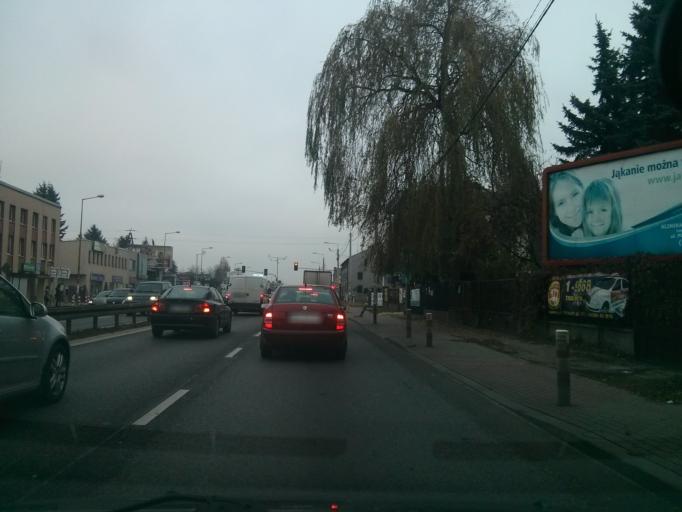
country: PL
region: Masovian Voivodeship
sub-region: Powiat pruszkowski
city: Raszyn
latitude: 52.1583
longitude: 20.9250
